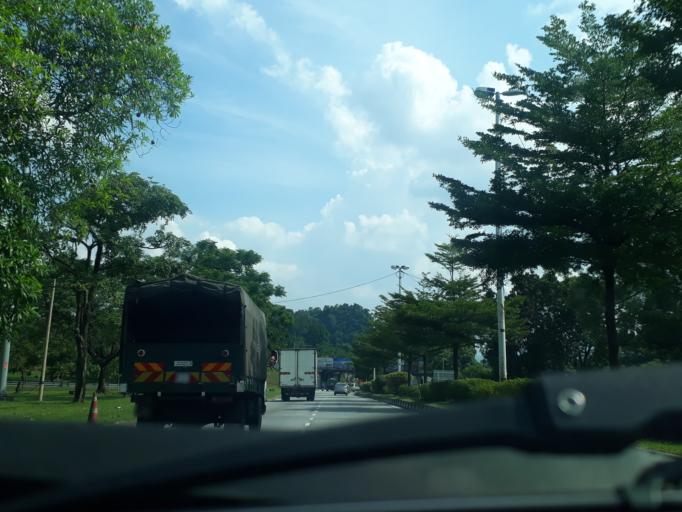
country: MY
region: Perak
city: Ipoh
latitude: 4.6380
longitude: 101.0921
